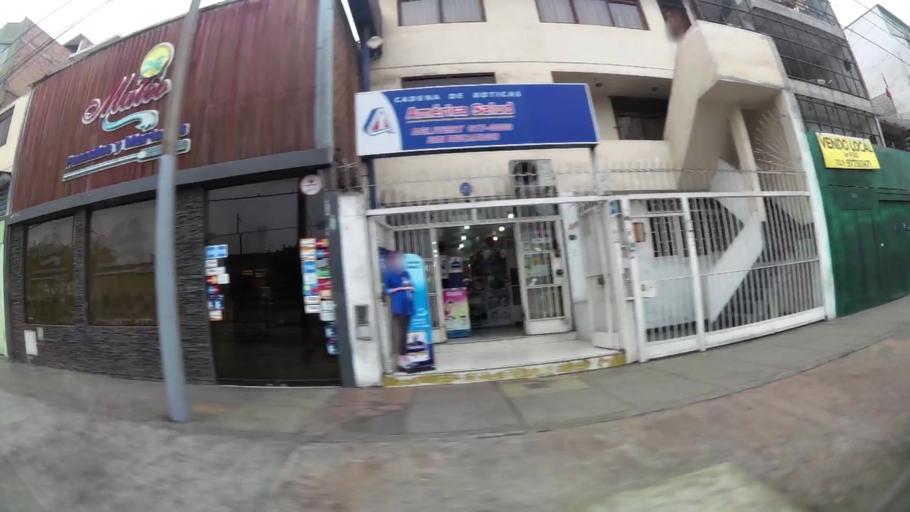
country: PE
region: Callao
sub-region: Callao
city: Callao
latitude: -12.0791
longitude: -77.0874
